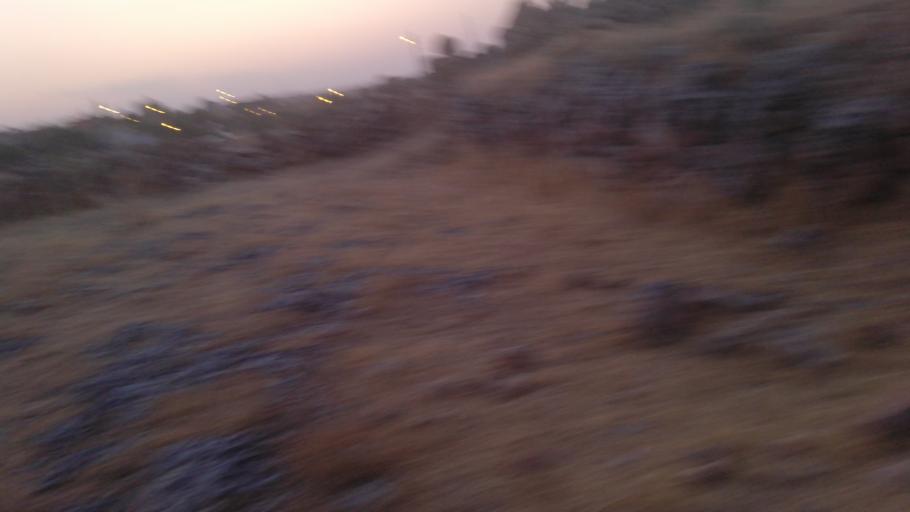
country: TR
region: Mardin
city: Kindirip
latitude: 37.4480
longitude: 41.2253
